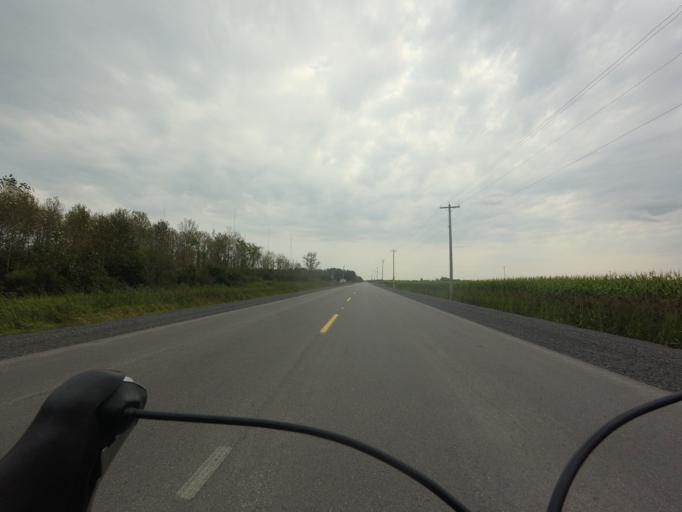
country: CA
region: Ontario
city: Bells Corners
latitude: 45.2186
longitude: -75.7733
